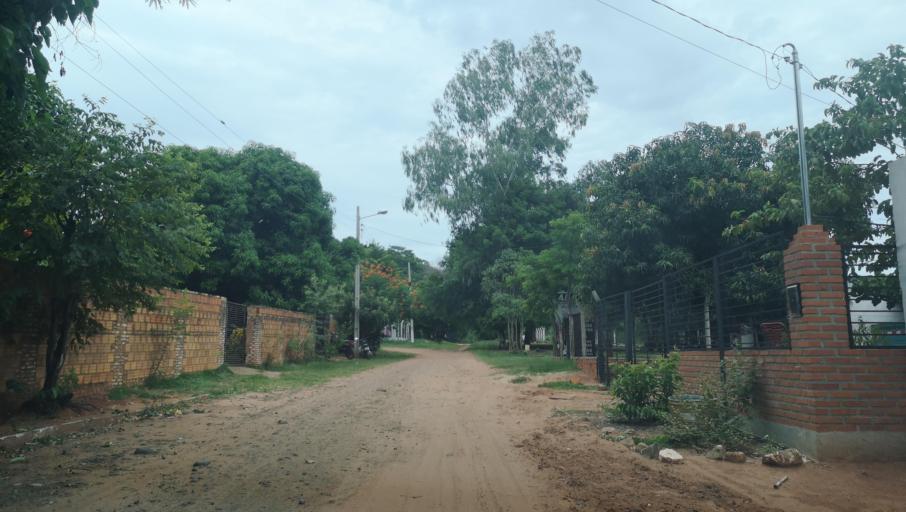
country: PY
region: San Pedro
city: Capiibary
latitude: -24.7284
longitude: -56.0147
